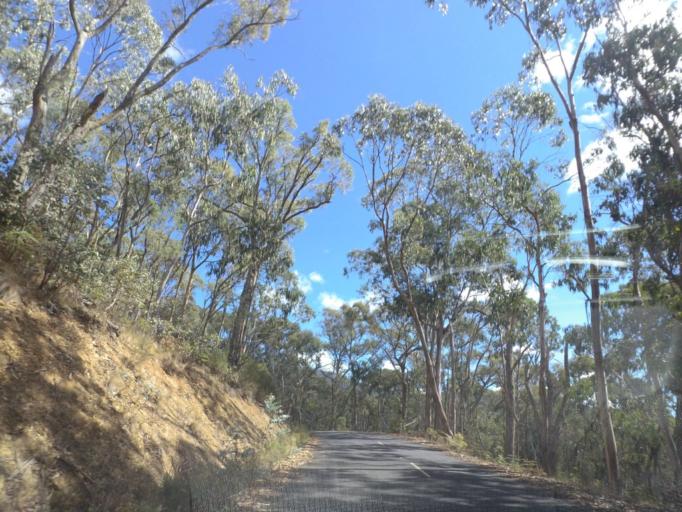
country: AU
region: Victoria
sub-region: Murrindindi
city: Alexandra
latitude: -37.3362
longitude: 145.9603
